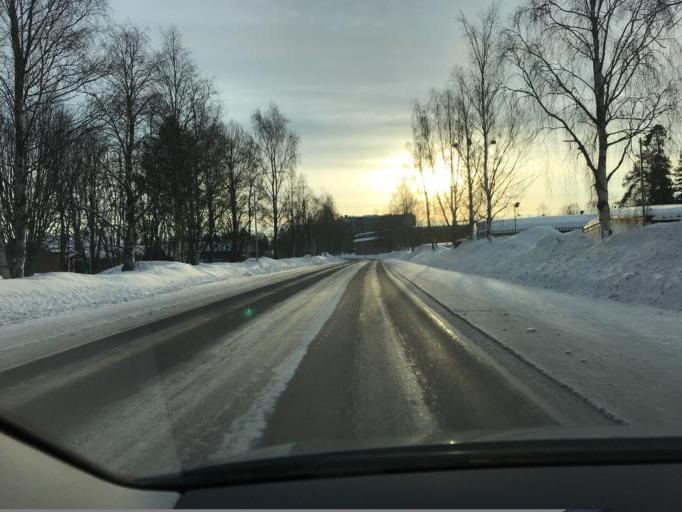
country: SE
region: Norrbotten
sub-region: Lulea Kommun
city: Bergnaset
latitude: 65.6033
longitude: 22.1227
